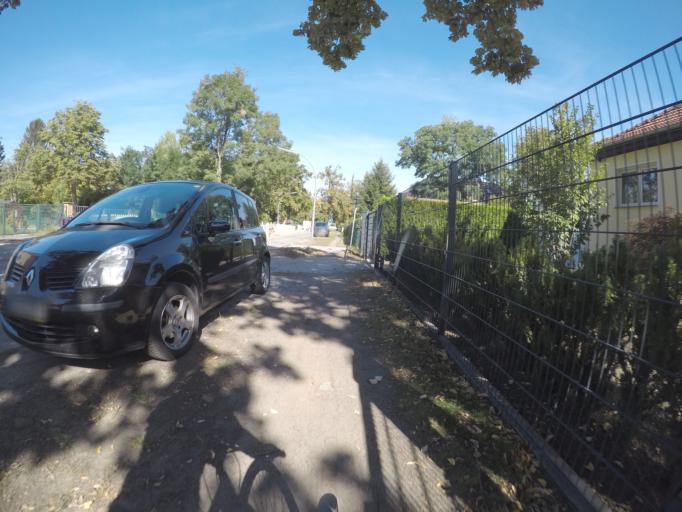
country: DE
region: Brandenburg
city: Hennigsdorf
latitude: 52.6121
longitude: 13.2174
